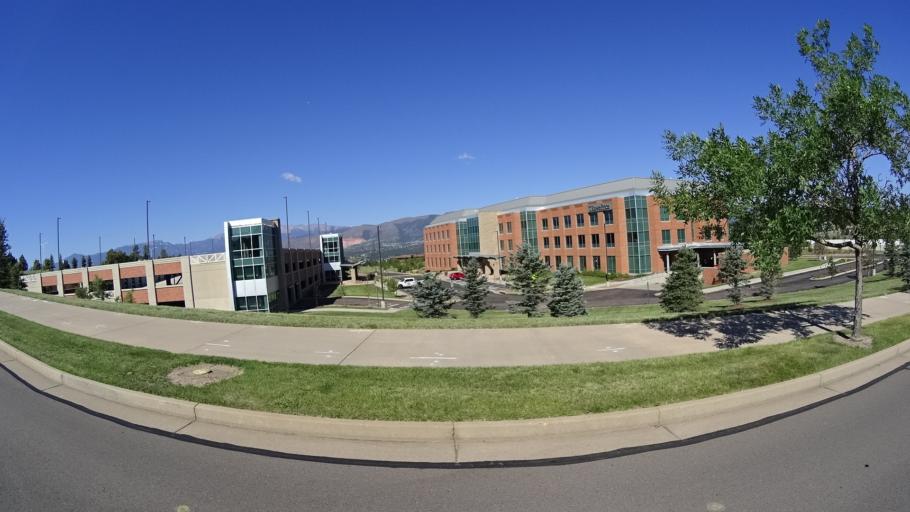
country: US
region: Colorado
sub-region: El Paso County
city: Air Force Academy
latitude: 38.9680
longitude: -104.7850
